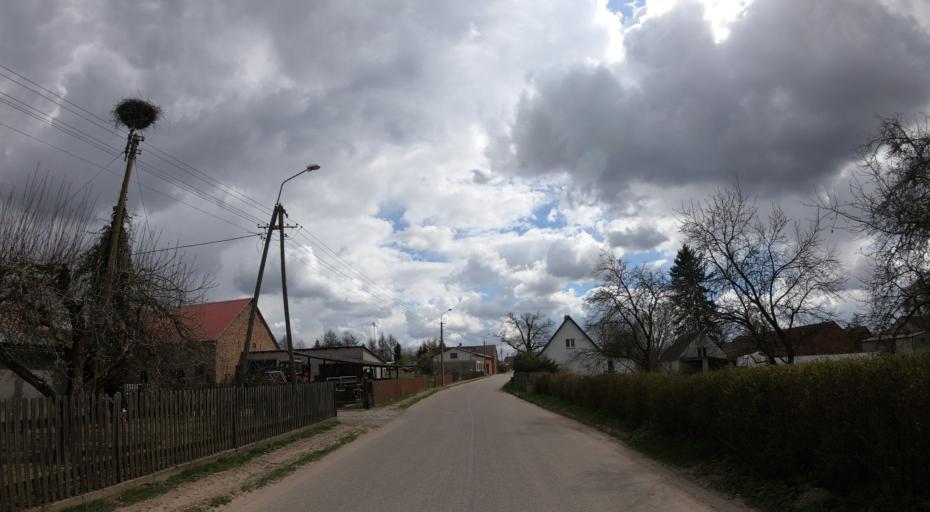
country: PL
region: West Pomeranian Voivodeship
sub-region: Powiat drawski
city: Drawsko Pomorskie
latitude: 53.5263
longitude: 15.8867
